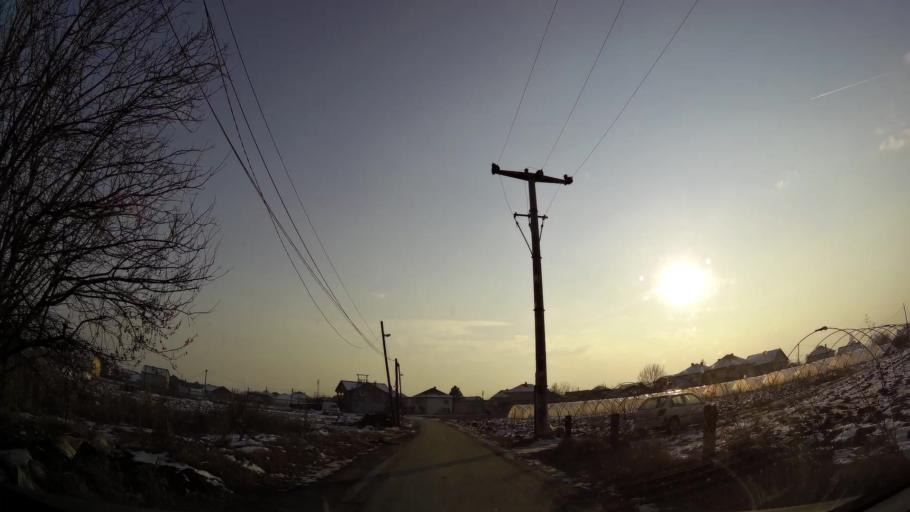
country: MK
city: Creshevo
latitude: 42.0254
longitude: 21.5197
